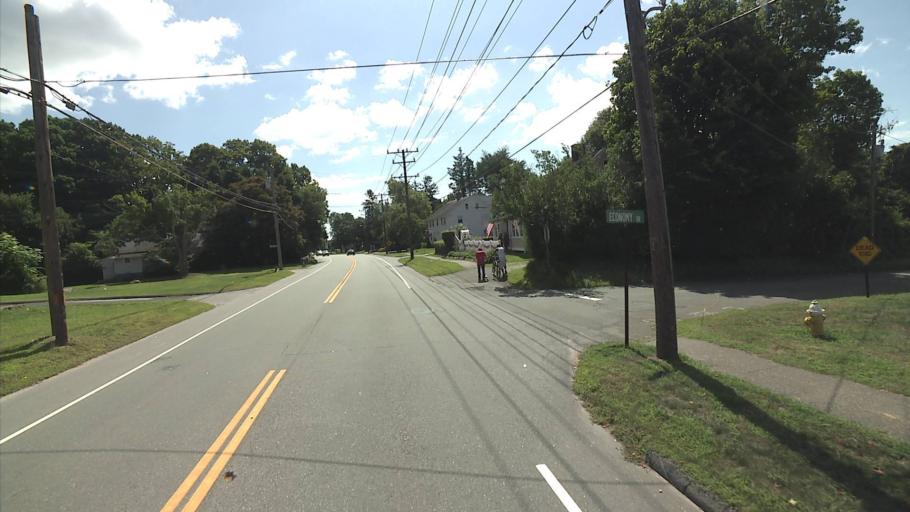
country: US
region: Connecticut
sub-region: Middlesex County
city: Westbrook Center
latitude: 41.2825
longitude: -72.4394
